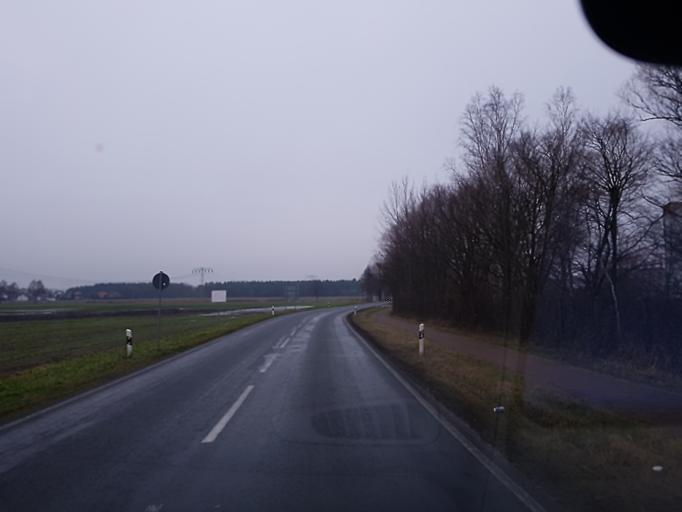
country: DE
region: Brandenburg
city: Lubbenau
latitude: 51.8437
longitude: 13.9495
